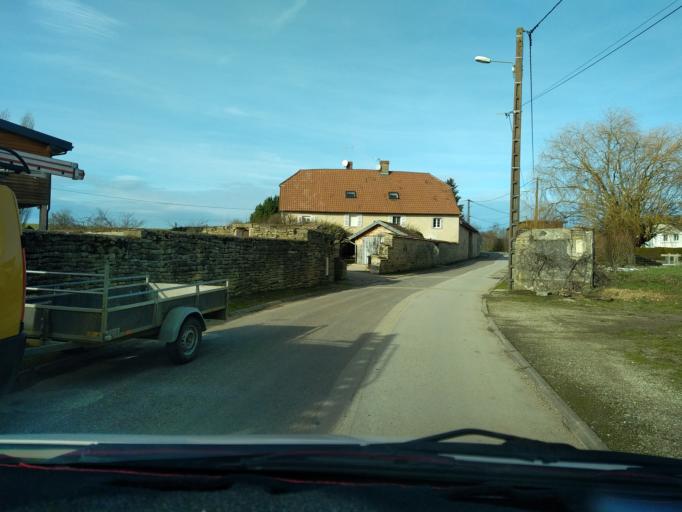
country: FR
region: Franche-Comte
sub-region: Departement de la Haute-Saone
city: Marnay
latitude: 47.3222
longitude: 5.6838
